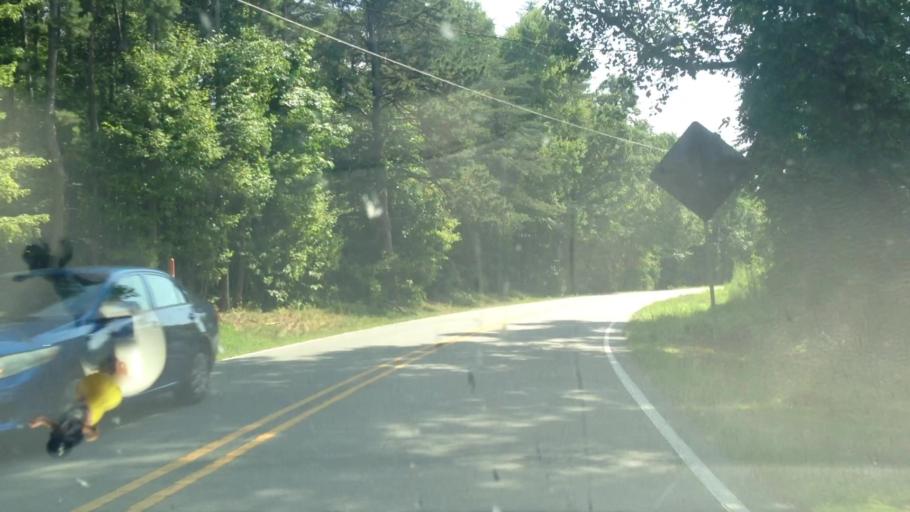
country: US
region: North Carolina
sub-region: Stokes County
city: Walnut Cove
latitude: 36.3075
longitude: -80.0467
